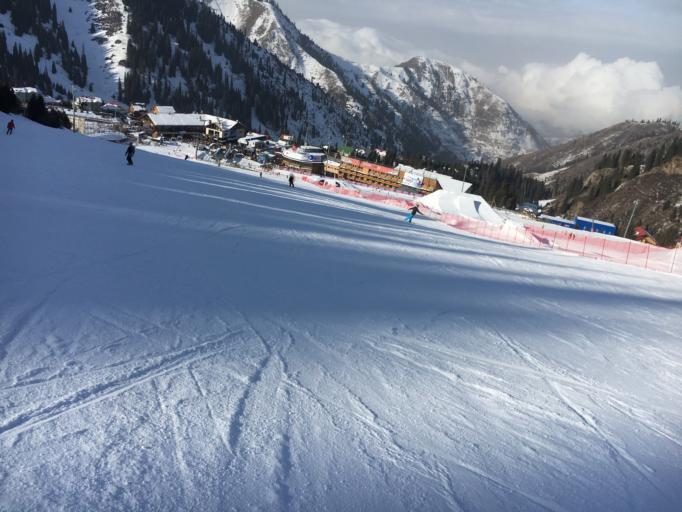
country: KZ
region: Almaty Qalasy
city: Almaty
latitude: 43.1262
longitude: 77.0856
